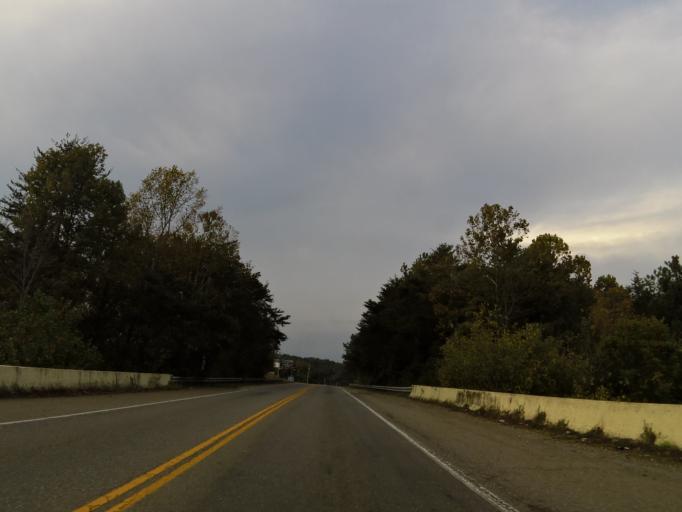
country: US
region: Tennessee
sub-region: Monroe County
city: Vonore
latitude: 35.5791
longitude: -84.2726
